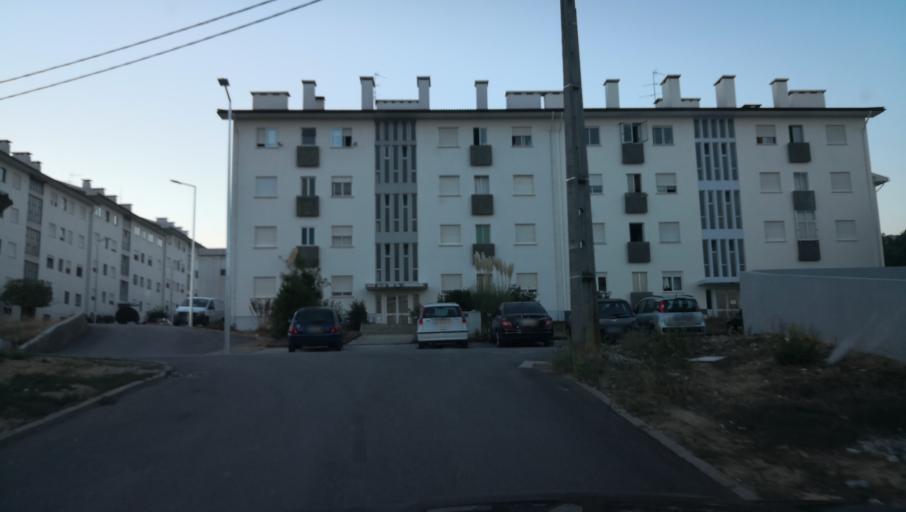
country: PT
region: Vila Real
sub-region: Vila Real
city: Vila Real
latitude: 41.3098
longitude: -7.7672
